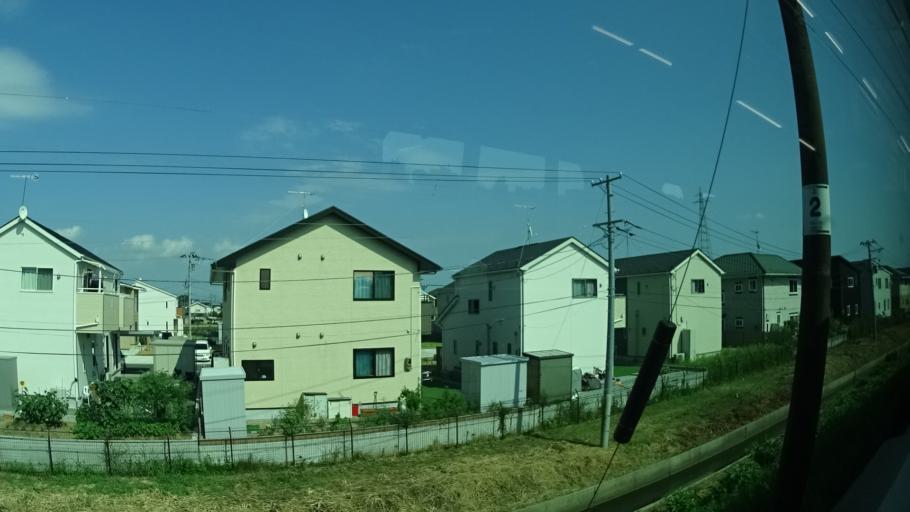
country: JP
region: Miyagi
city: Wakuya
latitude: 38.4813
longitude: 141.0992
